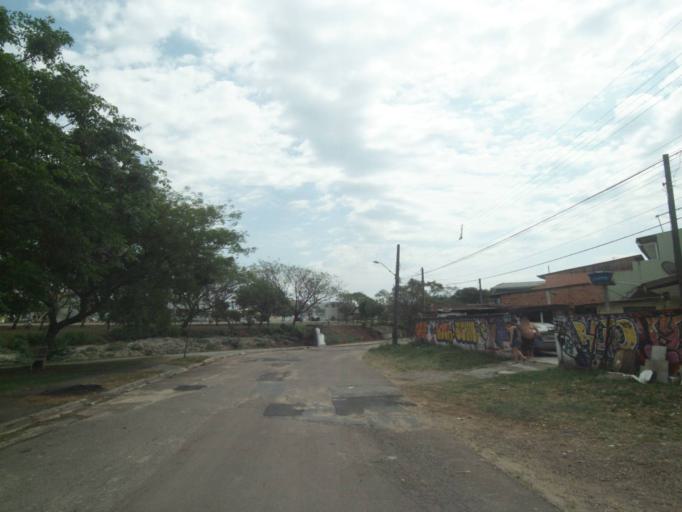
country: BR
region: Parana
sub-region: Sao Jose Dos Pinhais
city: Sao Jose dos Pinhais
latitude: -25.5270
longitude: -49.2629
